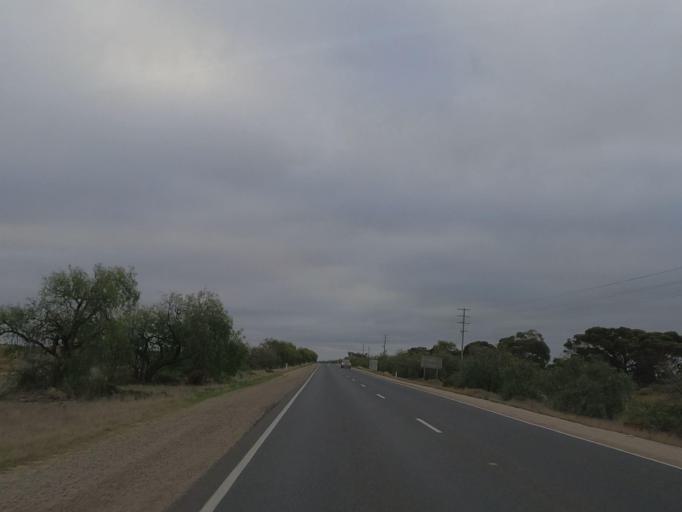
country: AU
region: Victoria
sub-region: Swan Hill
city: Swan Hill
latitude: -35.4487
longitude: 143.6225
